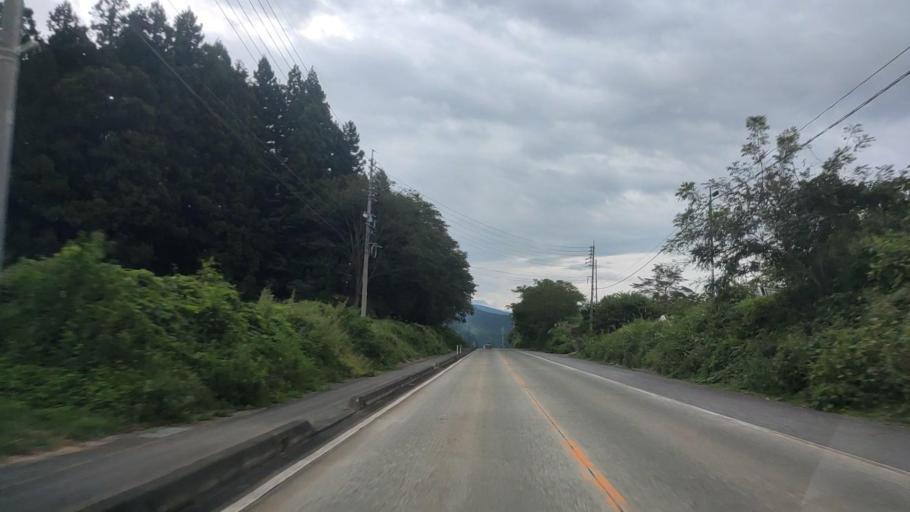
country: JP
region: Nagano
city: Iiyama
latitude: 36.8889
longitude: 138.4086
